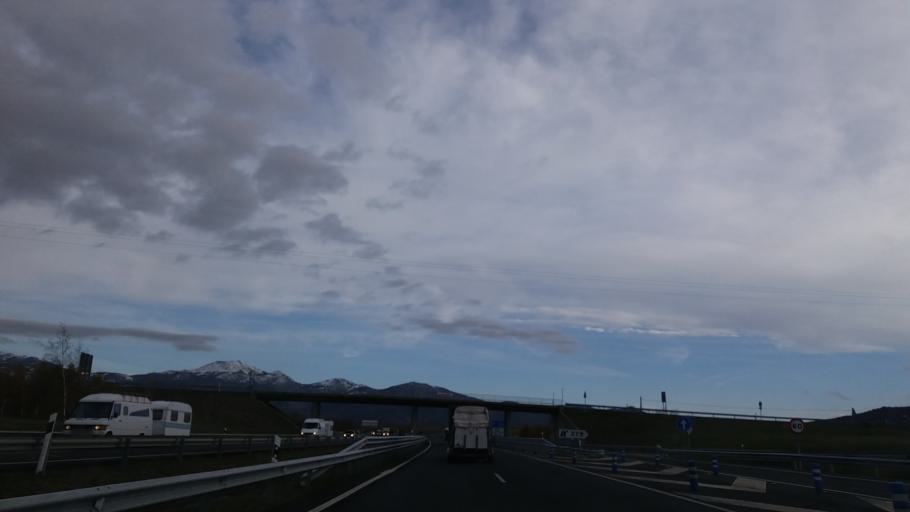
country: ES
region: Basque Country
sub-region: Provincia de Alava
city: Salvatierra
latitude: 42.8454
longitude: -2.3814
